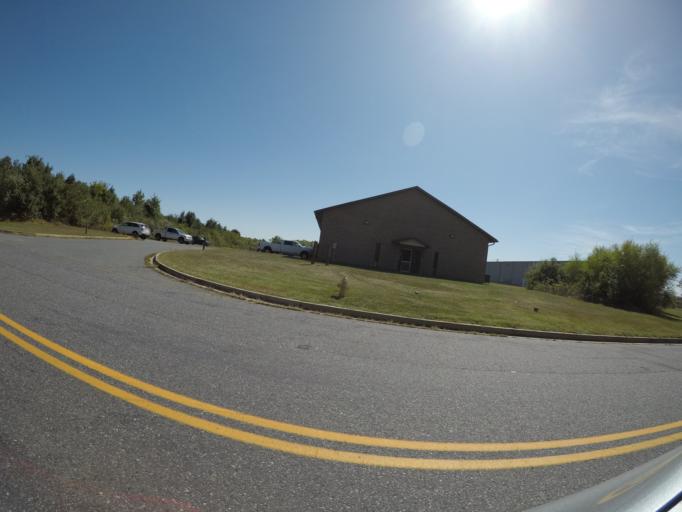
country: US
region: Maryland
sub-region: Harford County
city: Perryman
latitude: 39.4906
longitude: -76.1982
